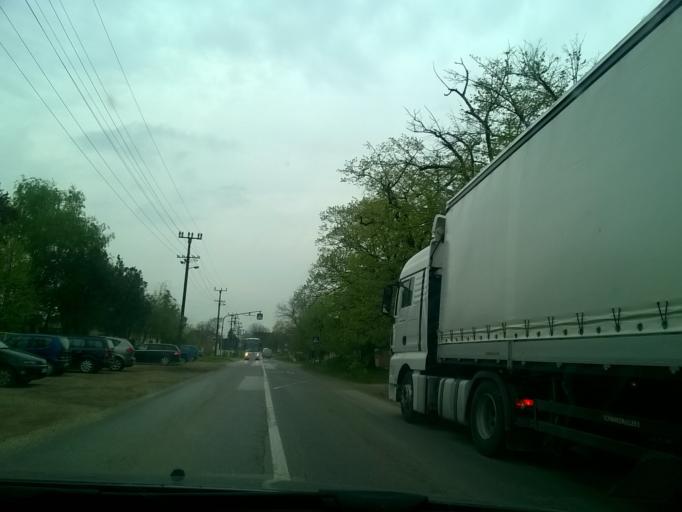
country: RS
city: Hrtkovci
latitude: 44.8781
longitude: 19.7701
